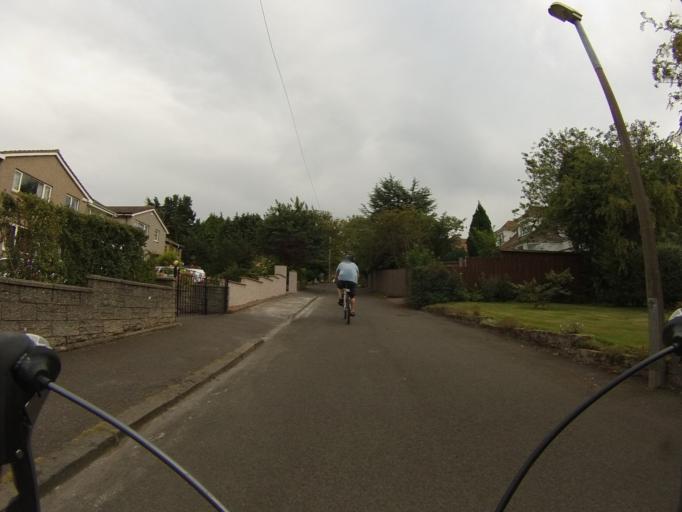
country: GB
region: Scotland
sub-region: Edinburgh
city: Colinton
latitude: 55.9027
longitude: -3.2648
